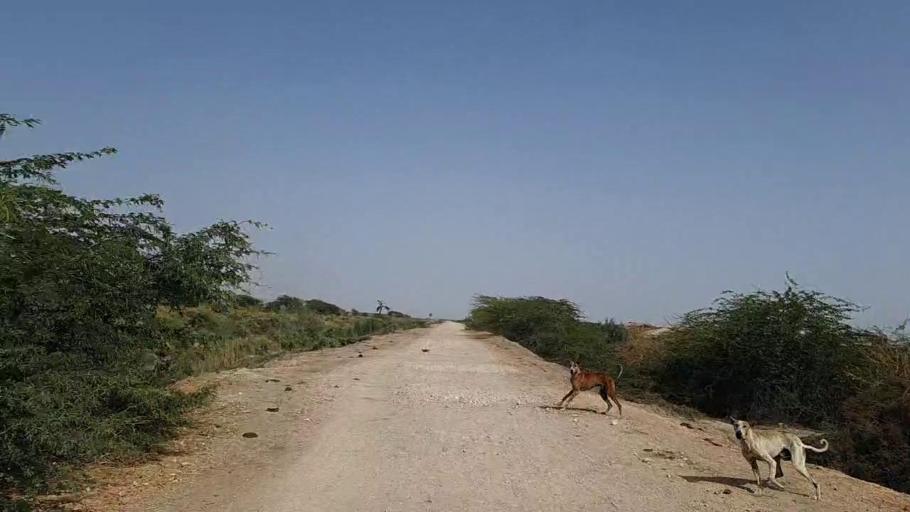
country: PK
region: Sindh
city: Jati
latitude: 24.3608
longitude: 68.2841
